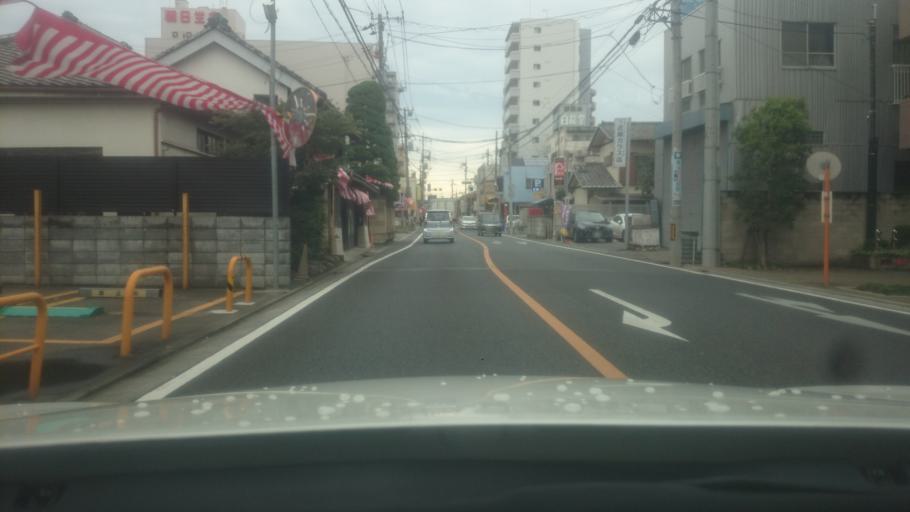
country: JP
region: Saitama
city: Kawagoe
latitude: 35.9072
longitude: 139.4866
